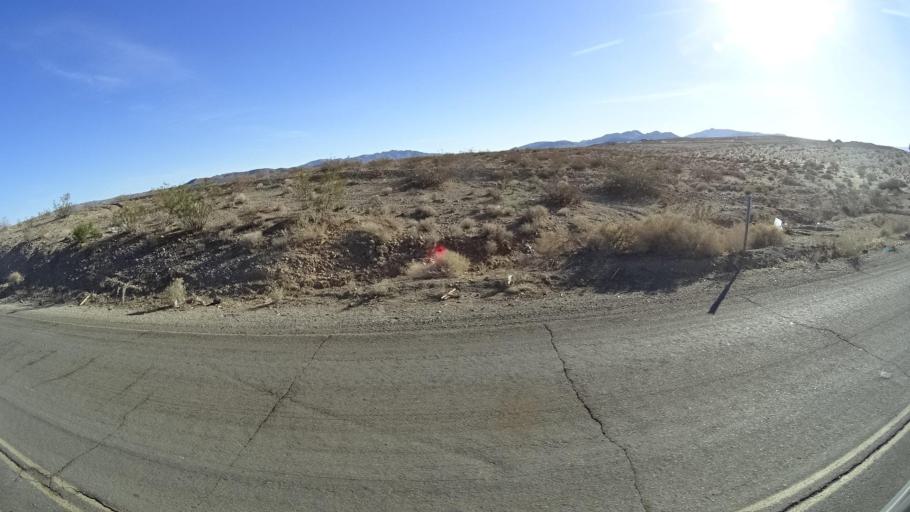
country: US
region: California
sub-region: Kern County
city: China Lake Acres
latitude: 35.6080
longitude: -117.7325
